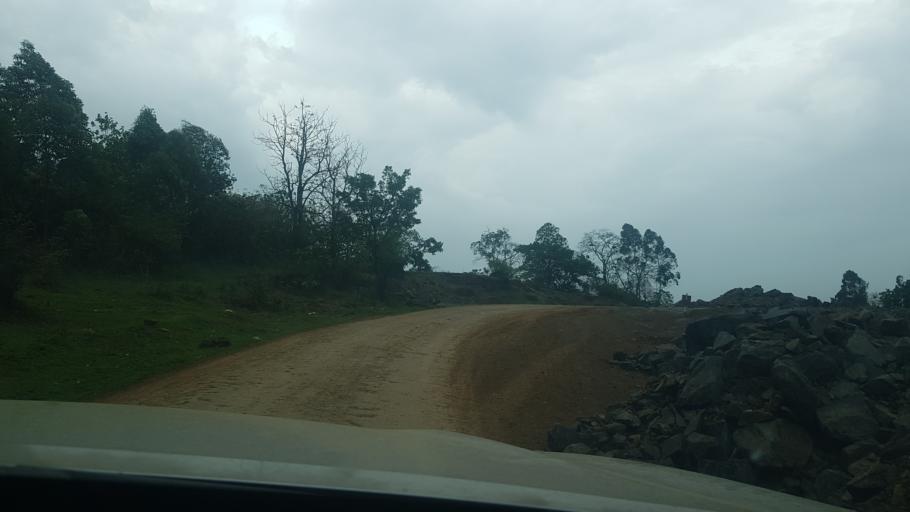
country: ET
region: Oromiya
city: Gore
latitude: 7.9200
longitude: 35.5147
